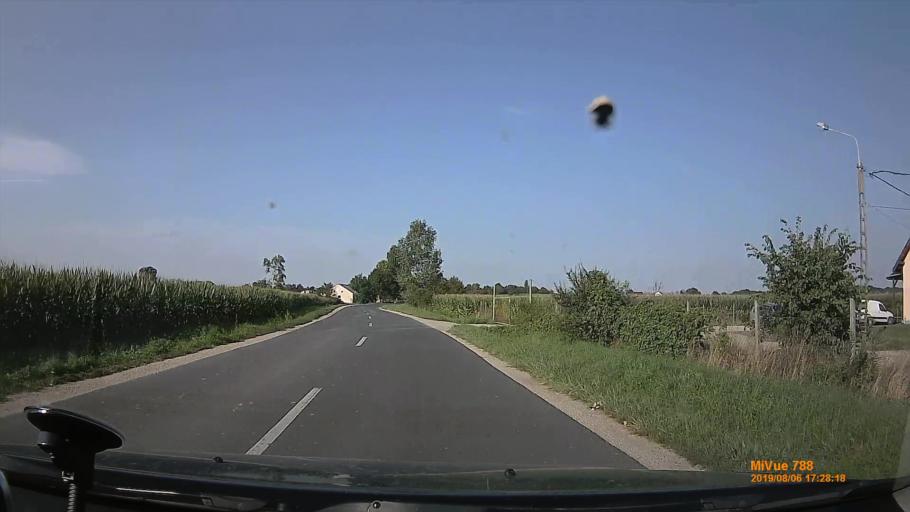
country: HR
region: Medimurska
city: Kotoriba
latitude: 46.3909
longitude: 16.8389
